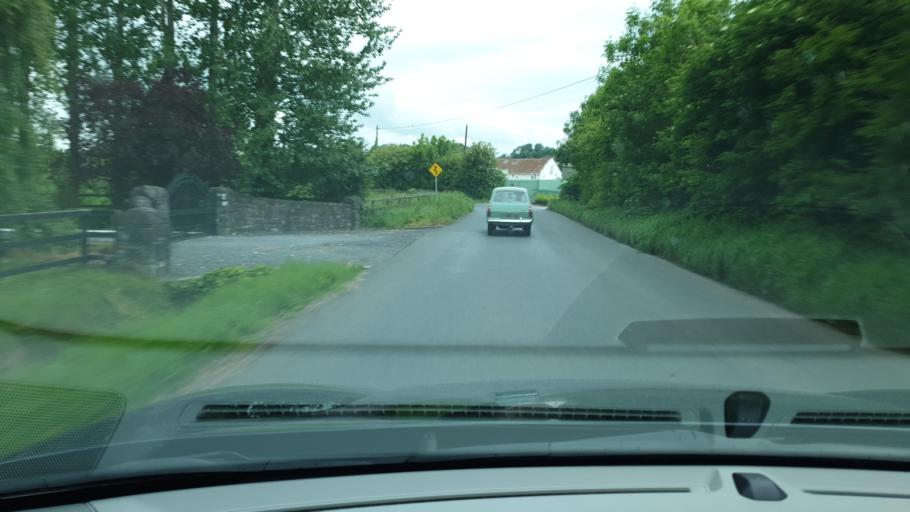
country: IE
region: Leinster
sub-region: An Mhi
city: Ashbourne
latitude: 53.5410
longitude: -6.4096
